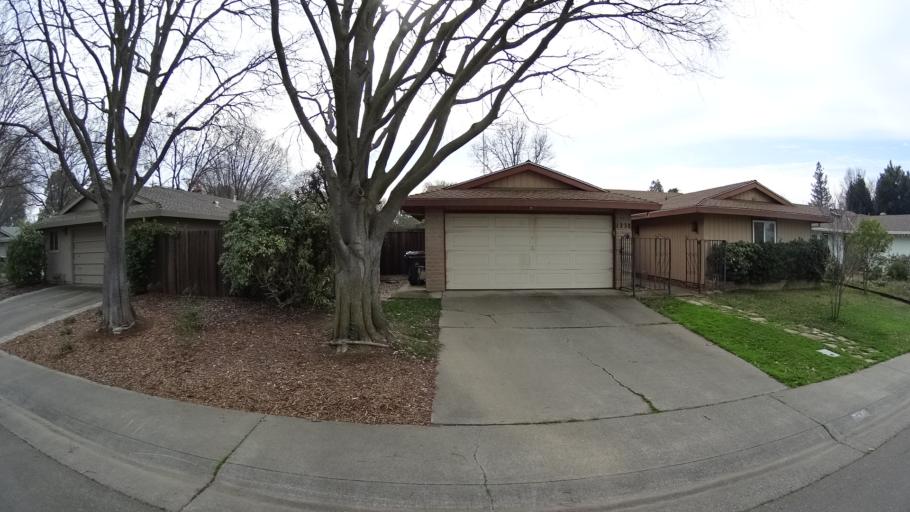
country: US
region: California
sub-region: Yolo County
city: Davis
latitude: 38.5587
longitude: -121.7367
